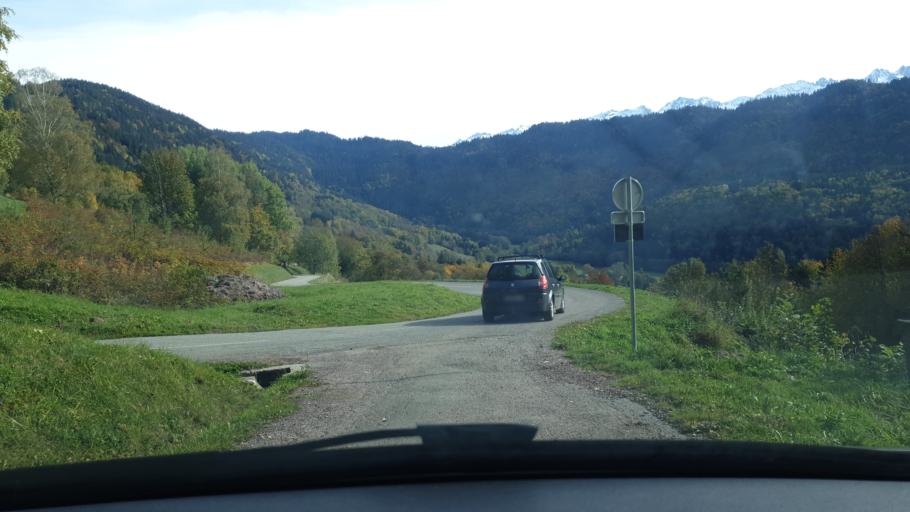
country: FR
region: Rhone-Alpes
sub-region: Departement de la Savoie
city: Aiton
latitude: 45.5005
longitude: 6.2244
